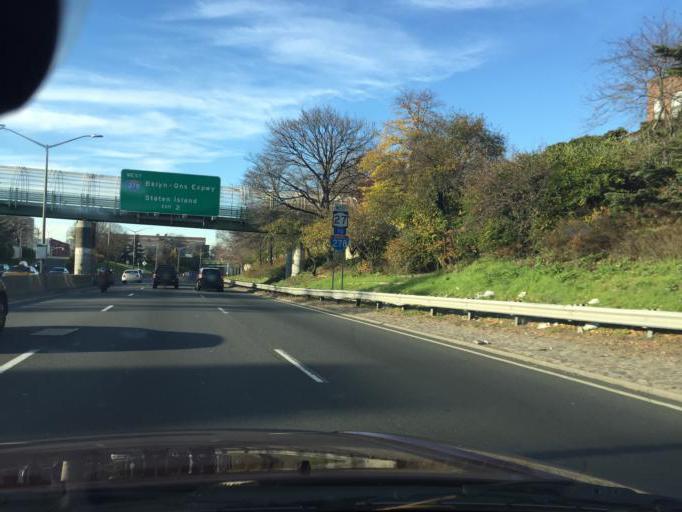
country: US
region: New York
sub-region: Kings County
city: Brooklyn
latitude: 40.6584
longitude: -73.9846
